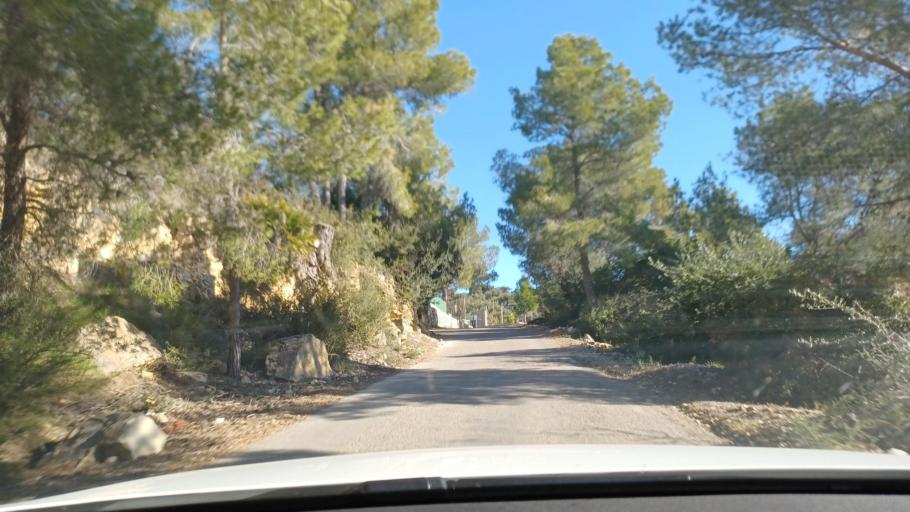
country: ES
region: Catalonia
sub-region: Provincia de Tarragona
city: Tortosa
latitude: 40.8141
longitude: 0.5553
